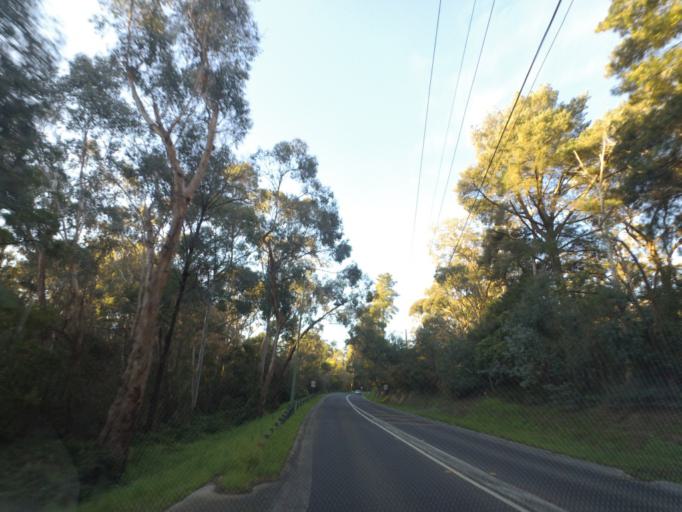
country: AU
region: Victoria
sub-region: Manningham
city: Park Orchards
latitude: -37.7845
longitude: 145.2077
